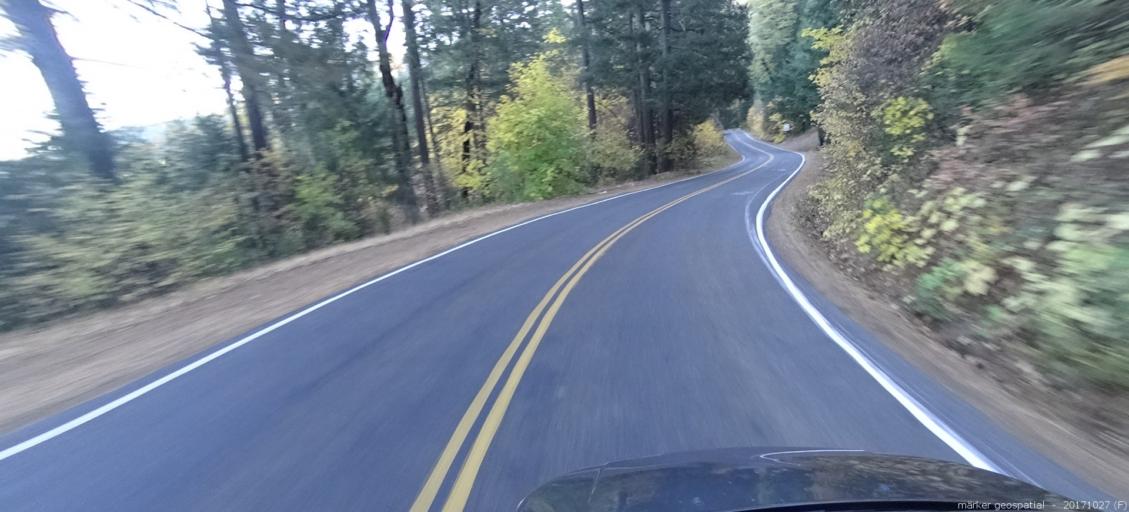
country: US
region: California
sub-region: Shasta County
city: Burney
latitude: 40.8987
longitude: -121.9023
